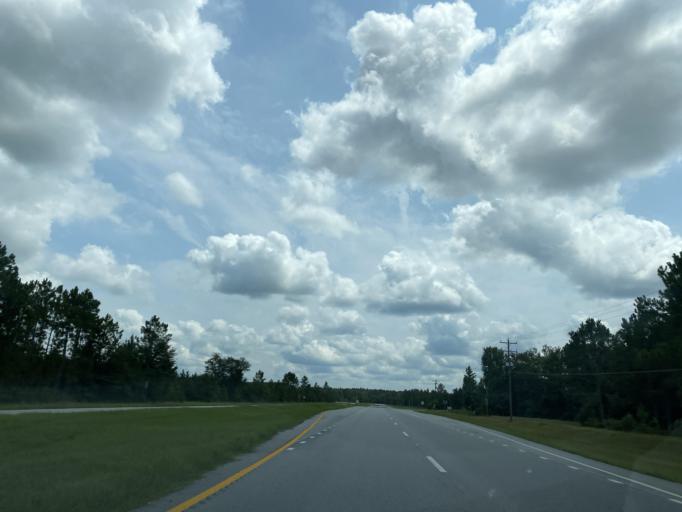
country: US
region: Georgia
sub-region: Ware County
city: Deenwood
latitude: 31.2841
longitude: -82.4513
